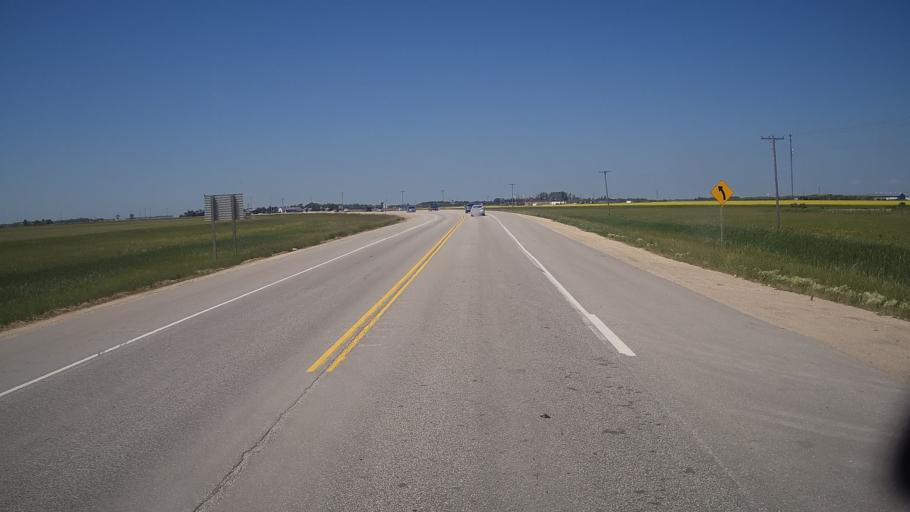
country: CA
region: Manitoba
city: Stonewall
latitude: 49.9882
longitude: -97.3120
